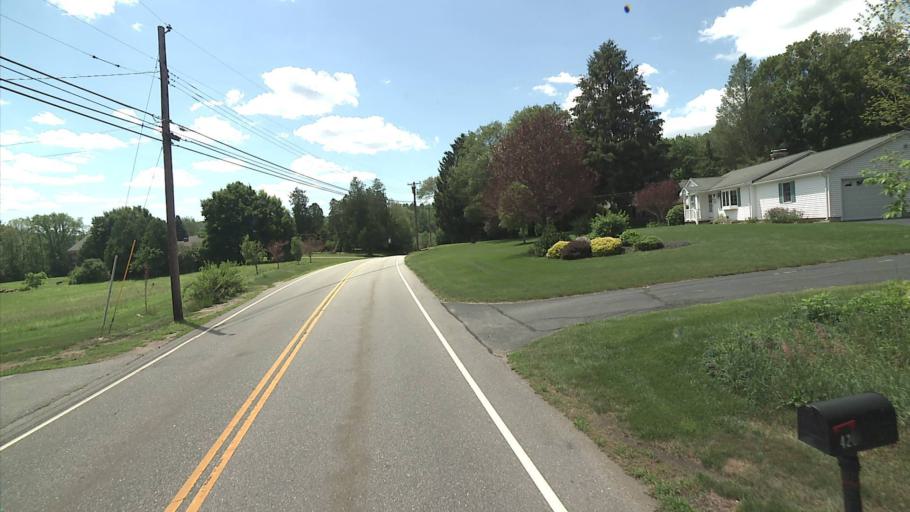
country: US
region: Connecticut
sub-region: Windham County
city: Quinebaug
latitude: 41.9972
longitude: -71.9869
